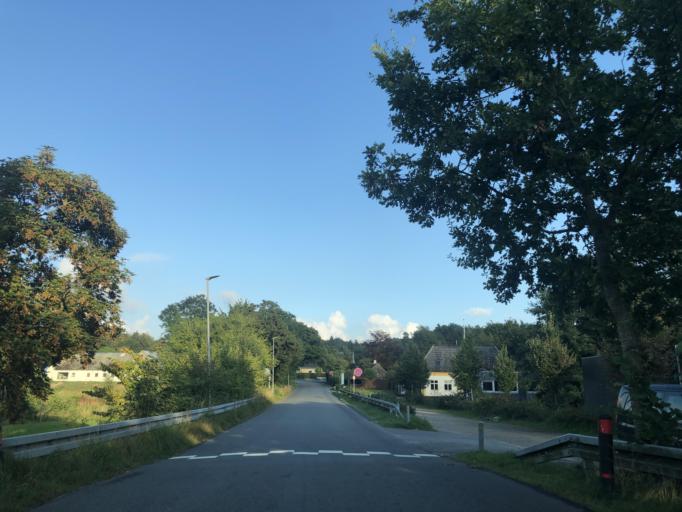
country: DK
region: North Denmark
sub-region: Alborg Kommune
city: Svenstrup
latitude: 56.9417
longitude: 9.8074
